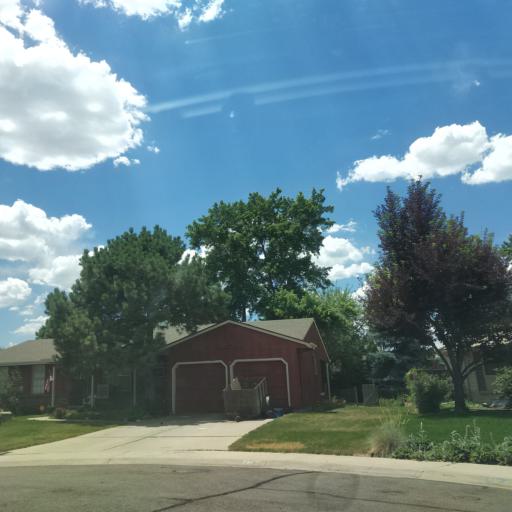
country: US
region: Colorado
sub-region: Jefferson County
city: Lakewood
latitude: 39.6850
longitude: -105.1018
